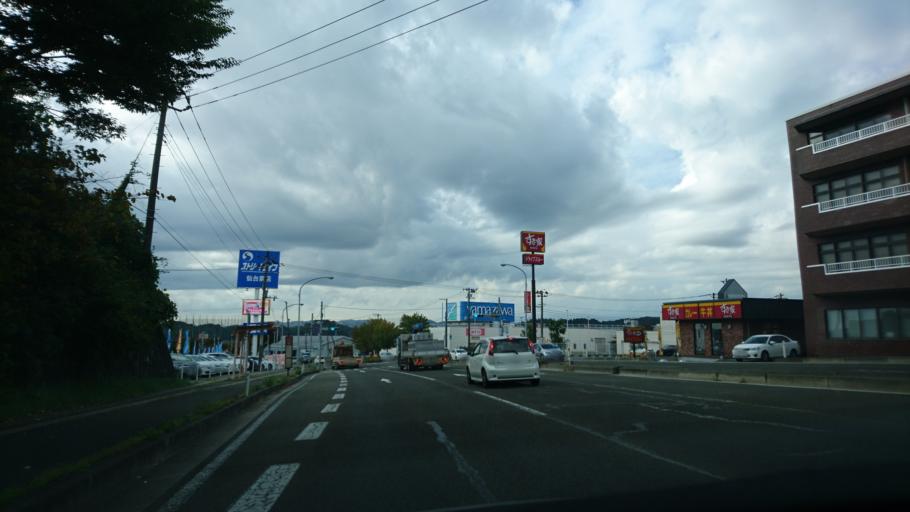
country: JP
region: Miyagi
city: Tomiya
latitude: 38.3572
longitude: 140.8716
